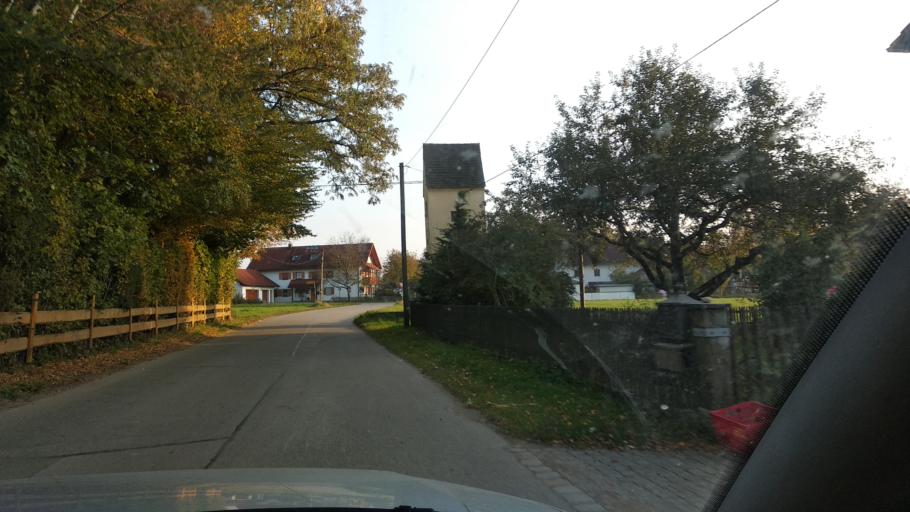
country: DE
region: Bavaria
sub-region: Upper Bavaria
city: Ottenhofen
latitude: 48.2020
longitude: 11.8946
